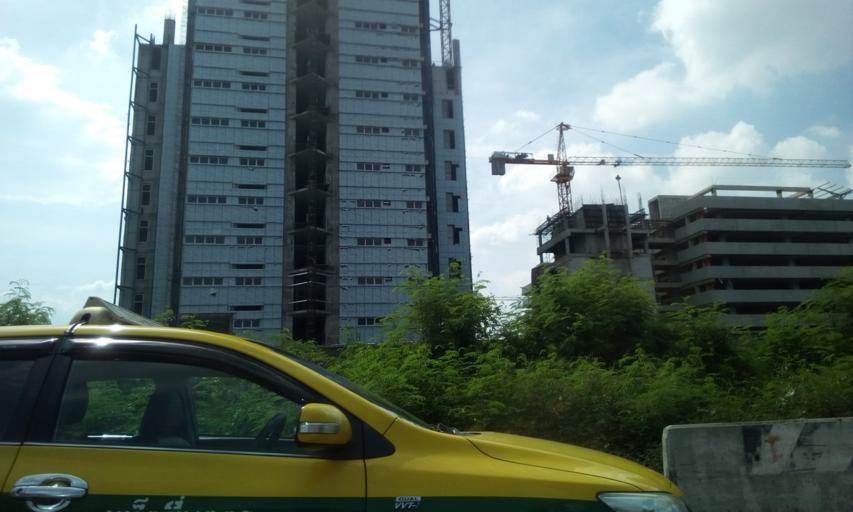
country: TH
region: Bangkok
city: Don Mueang
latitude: 13.9172
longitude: 100.5517
